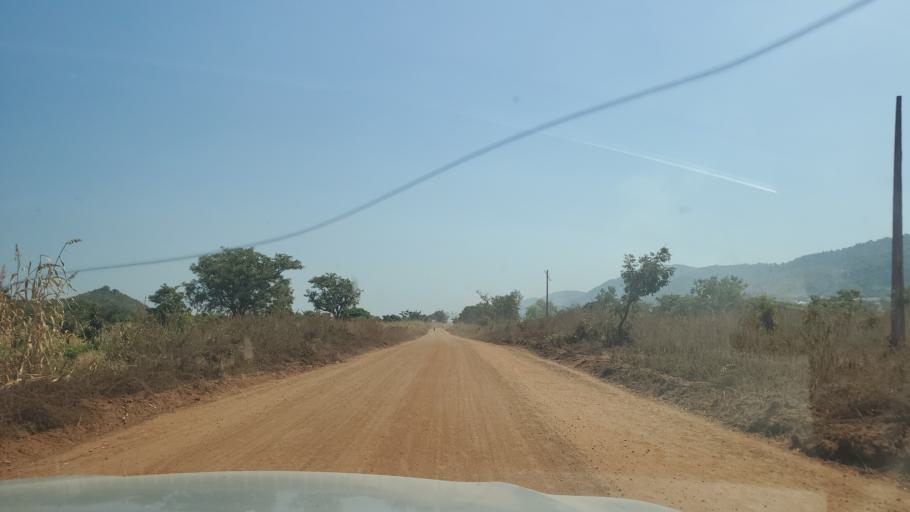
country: NG
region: Niger
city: Gawu Babangida
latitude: 9.2236
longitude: 6.8397
